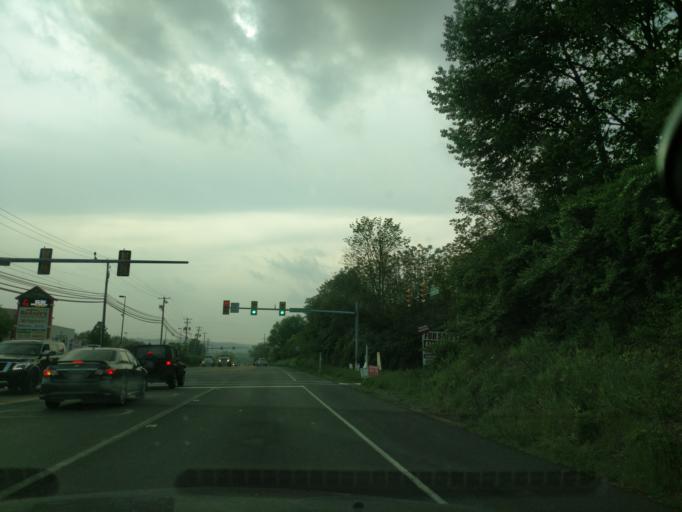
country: US
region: Pennsylvania
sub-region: Berks County
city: Wernersville
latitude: 40.3269
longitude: -76.0483
